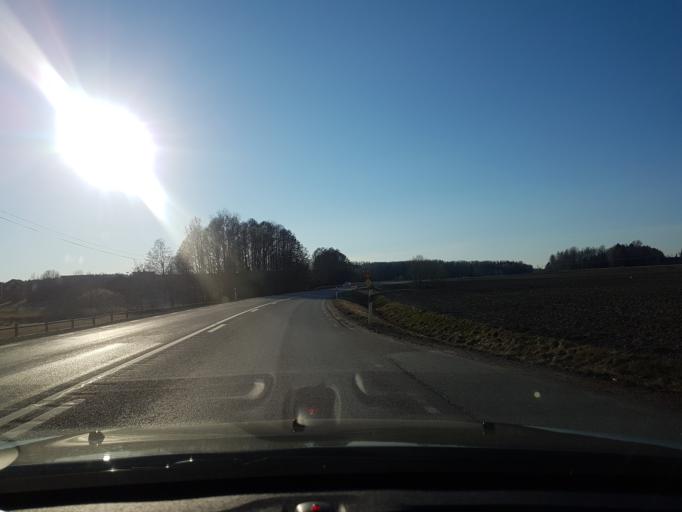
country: SE
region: Uppsala
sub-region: Heby Kommun
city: Morgongava
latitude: 59.9175
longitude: 17.0015
